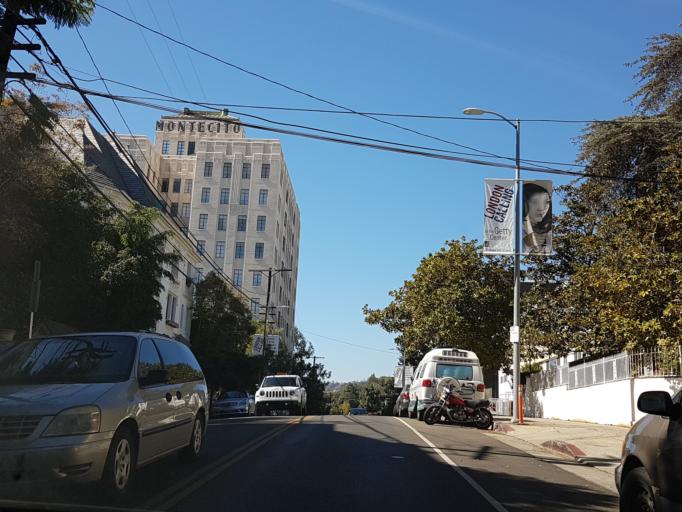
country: US
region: California
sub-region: Los Angeles County
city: Hollywood
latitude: 34.1052
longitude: -118.3342
